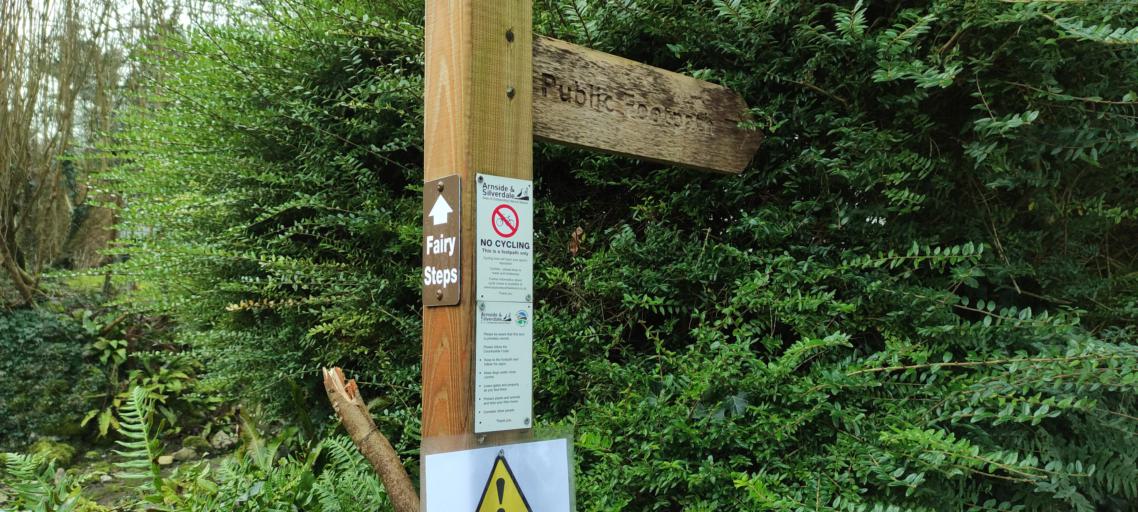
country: GB
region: England
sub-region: Cumbria
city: Milnthorpe
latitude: 54.2047
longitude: -2.7781
